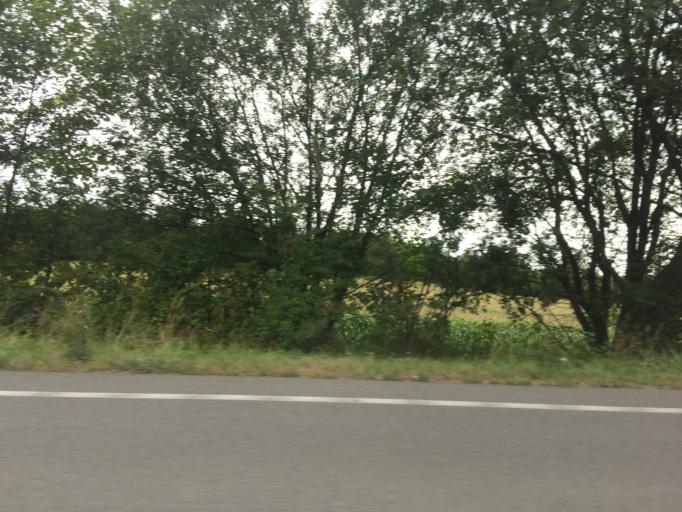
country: DE
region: Saxony
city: Wilsdruff
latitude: 51.0592
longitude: 13.5336
